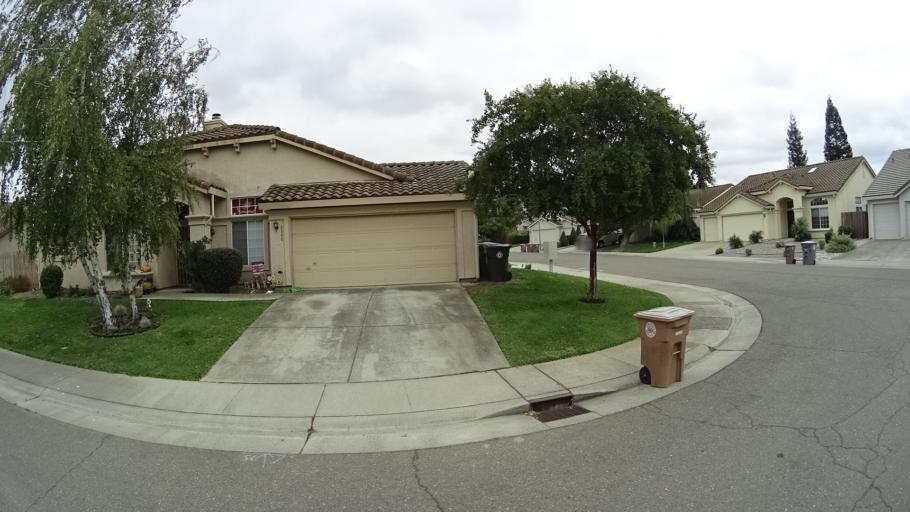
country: US
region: California
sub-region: Sacramento County
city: Laguna
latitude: 38.4193
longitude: -121.4530
